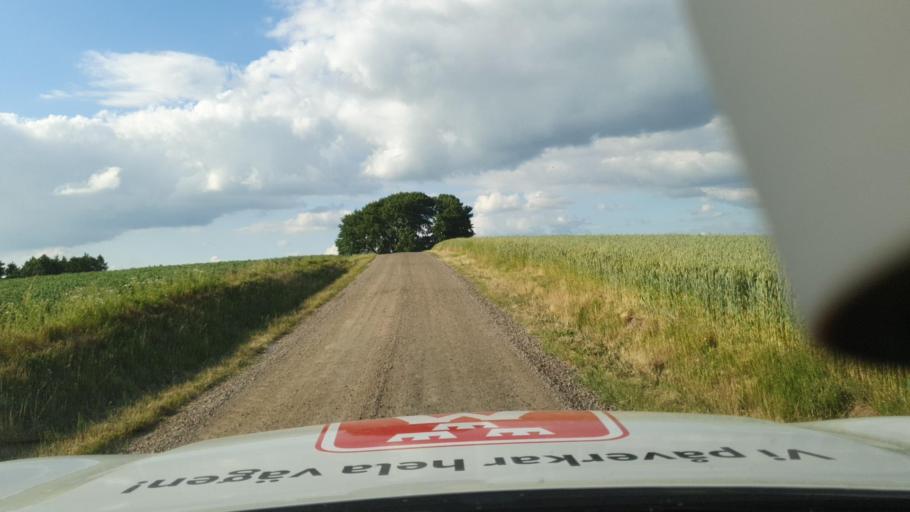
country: SE
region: Skane
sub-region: Skurups Kommun
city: Rydsgard
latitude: 55.4962
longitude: 13.5767
